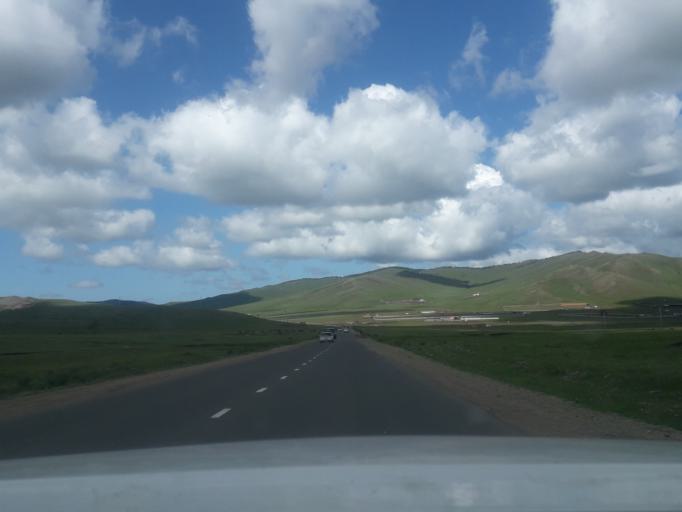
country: MN
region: Central Aimak
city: Ihsueuej
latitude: 48.1620
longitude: 106.4043
